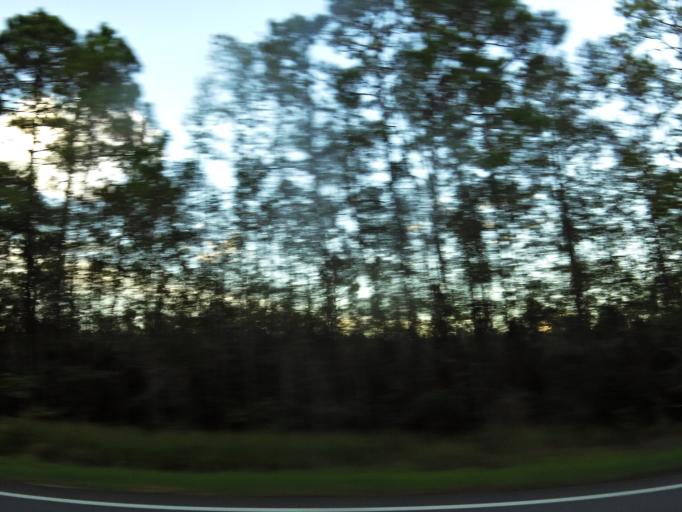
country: US
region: Georgia
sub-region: Echols County
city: Statenville
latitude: 30.7394
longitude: -83.0958
